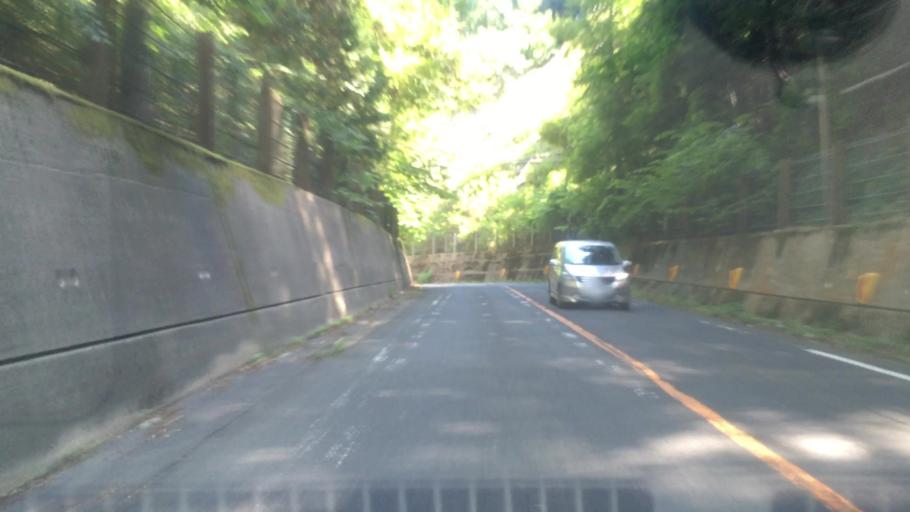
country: JP
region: Hyogo
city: Toyooka
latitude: 35.5934
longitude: 134.9134
